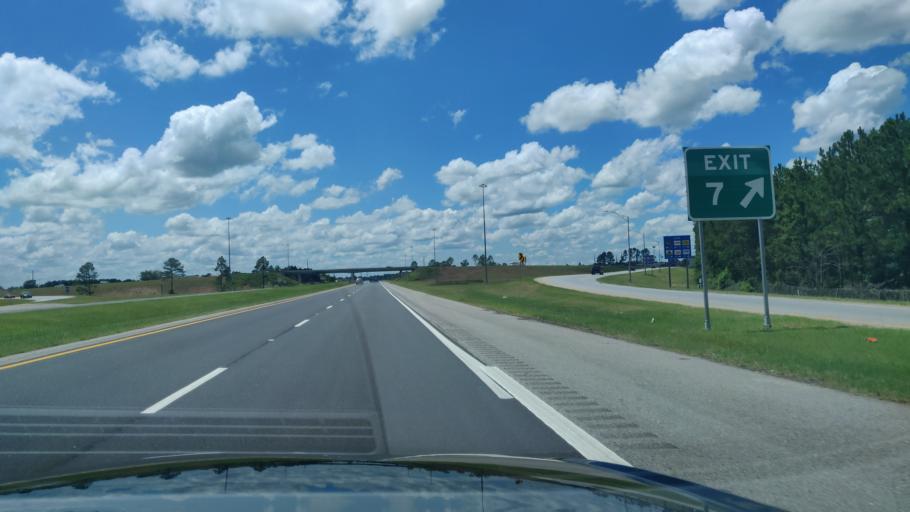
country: US
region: Georgia
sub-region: Dougherty County
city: Albany
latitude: 31.6162
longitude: -84.1996
